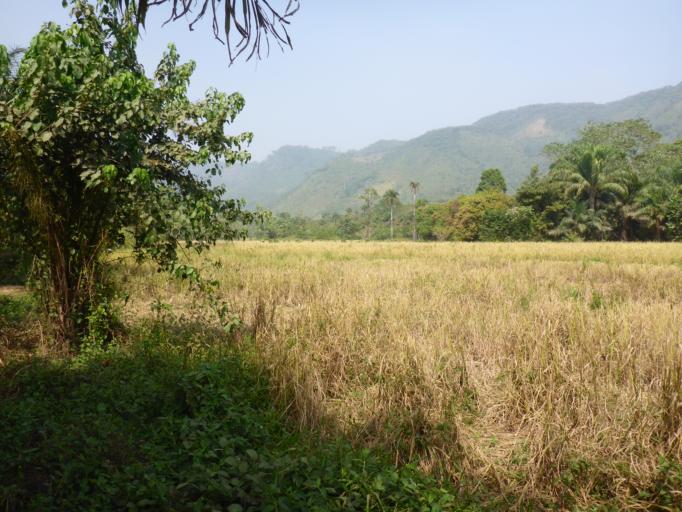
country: SL
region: Northern Province
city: Bumbuna
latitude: 8.9297
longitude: -11.7477
